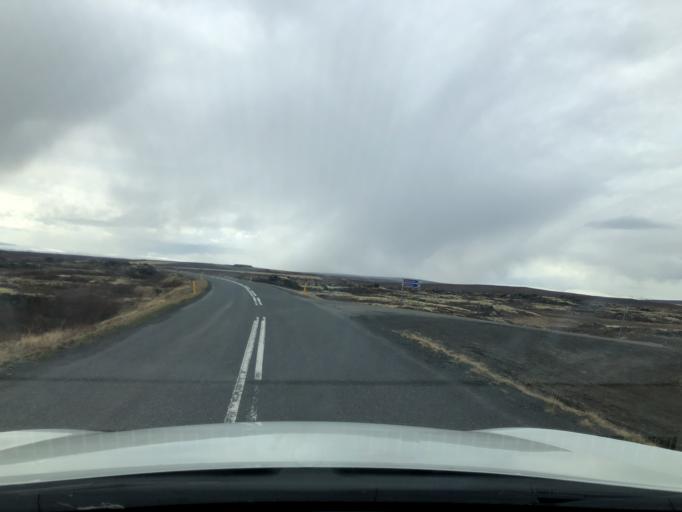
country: IS
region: Northeast
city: Laugar
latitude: 65.5716
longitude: -17.0544
